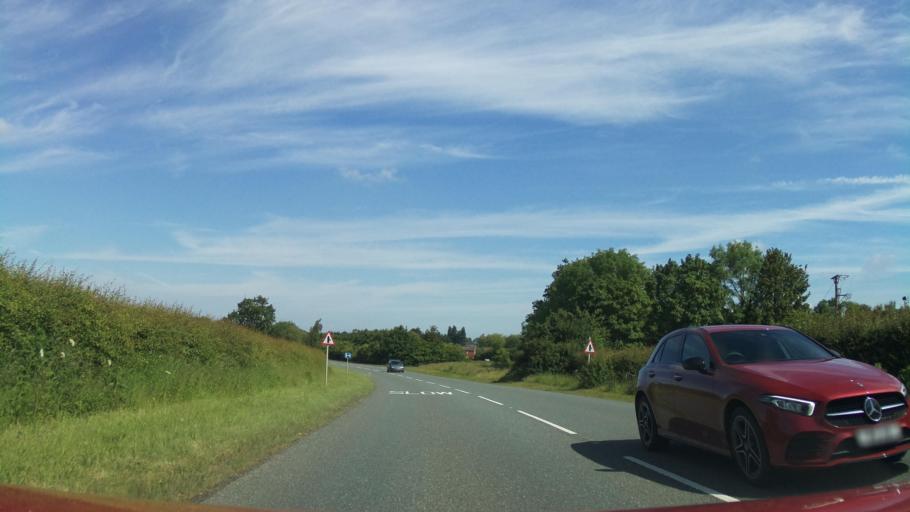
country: GB
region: England
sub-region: Lincolnshire
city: Skellingthorpe
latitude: 53.1638
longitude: -0.6387
